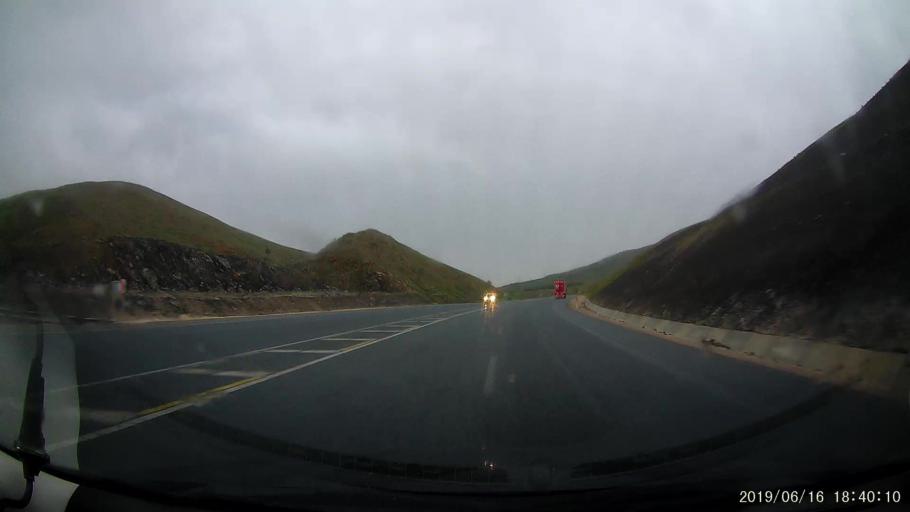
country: TR
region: Erzincan
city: Catalarmut
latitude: 39.8802
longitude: 39.1525
